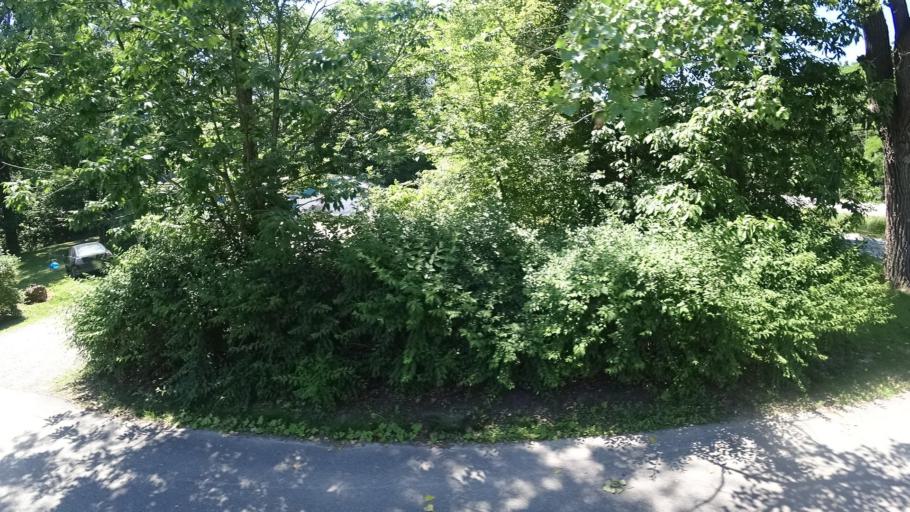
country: US
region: Indiana
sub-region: Porter County
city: Burns Harbor
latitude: 41.6156
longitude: -87.1253
